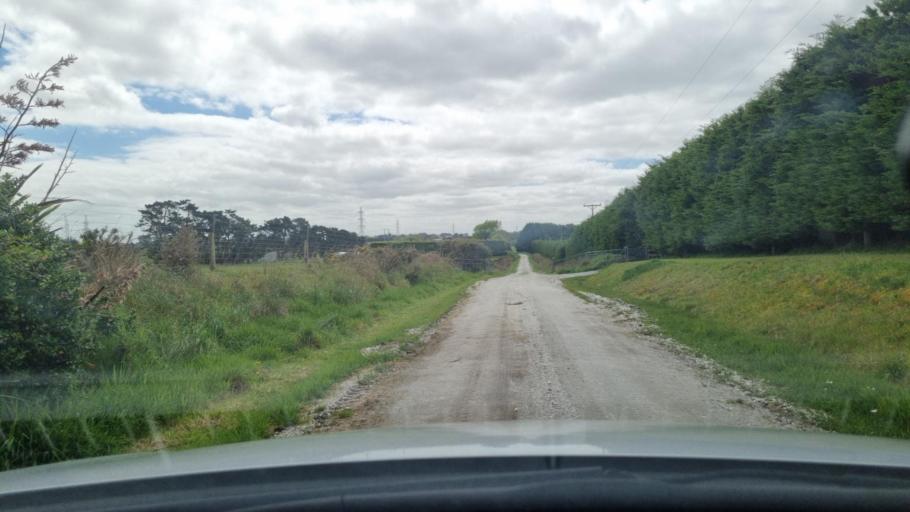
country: NZ
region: Southland
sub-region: Invercargill City
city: Invercargill
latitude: -46.3916
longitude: 168.4054
